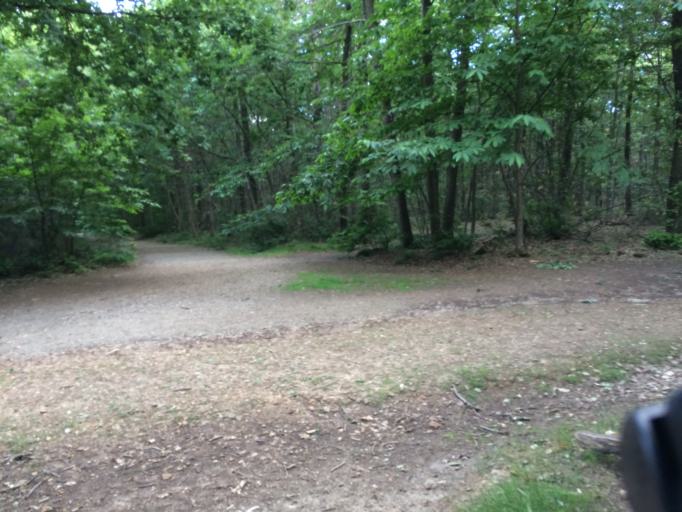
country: FR
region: Ile-de-France
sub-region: Departement des Hauts-de-Seine
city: Chatenay-Malabry
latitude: 48.7550
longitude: 2.2580
